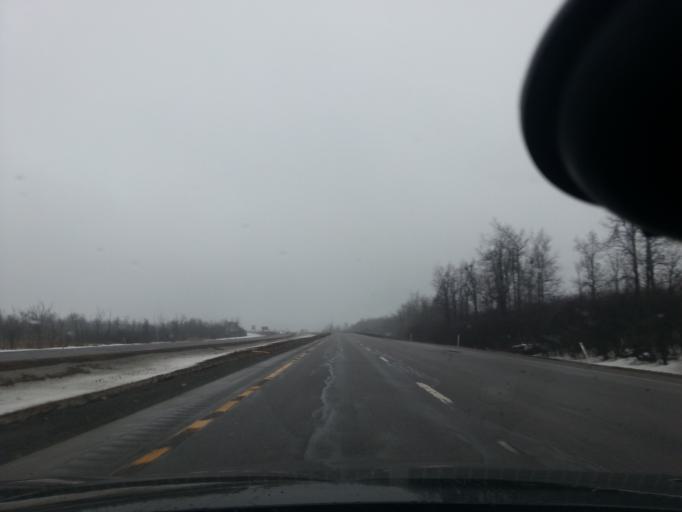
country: US
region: New York
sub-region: Jefferson County
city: Watertown
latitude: 44.0311
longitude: -75.9159
